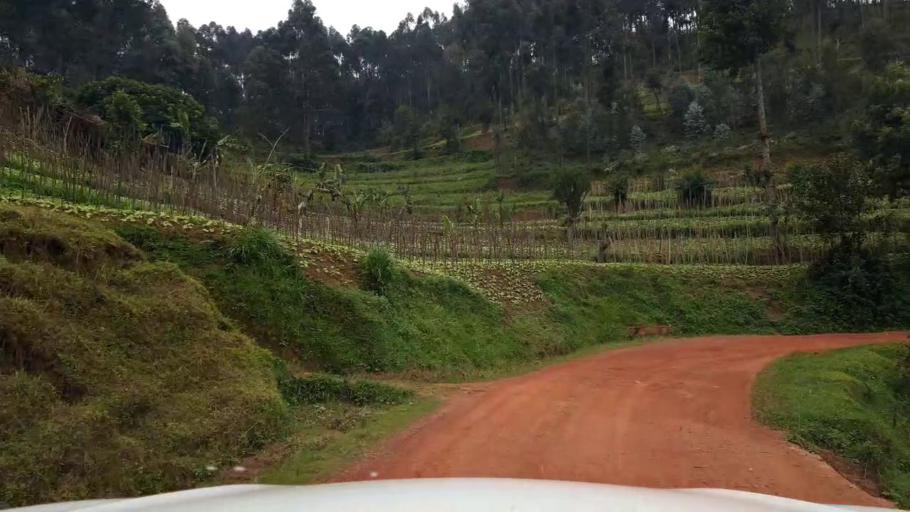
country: RW
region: Northern Province
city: Byumba
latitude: -1.5263
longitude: 29.9613
